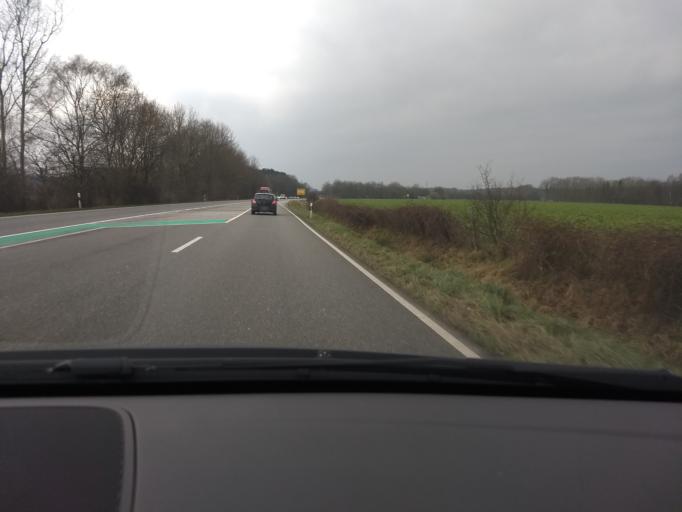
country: DE
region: North Rhine-Westphalia
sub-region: Regierungsbezirk Munster
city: Heiden
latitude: 51.8461
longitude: 6.9098
